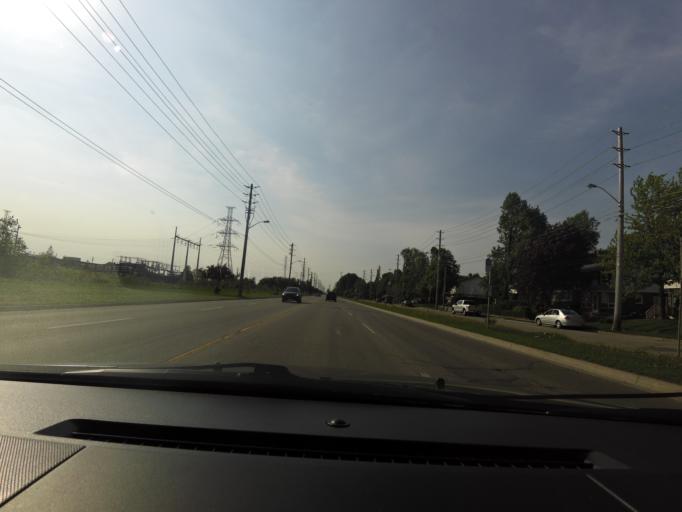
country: CA
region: Ontario
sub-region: Wellington County
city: Guelph
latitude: 43.5533
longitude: -80.2803
